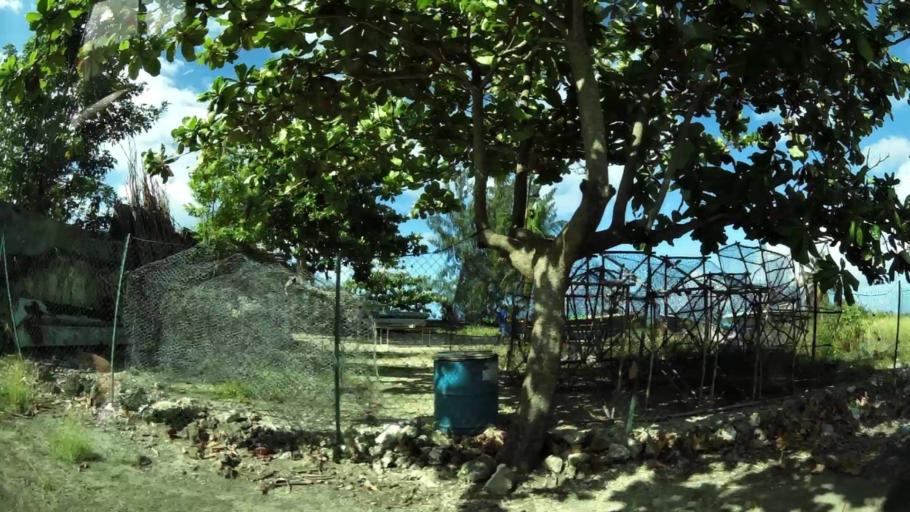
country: GP
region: Guadeloupe
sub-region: Guadeloupe
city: Port-Louis
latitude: 16.4149
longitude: -61.5330
